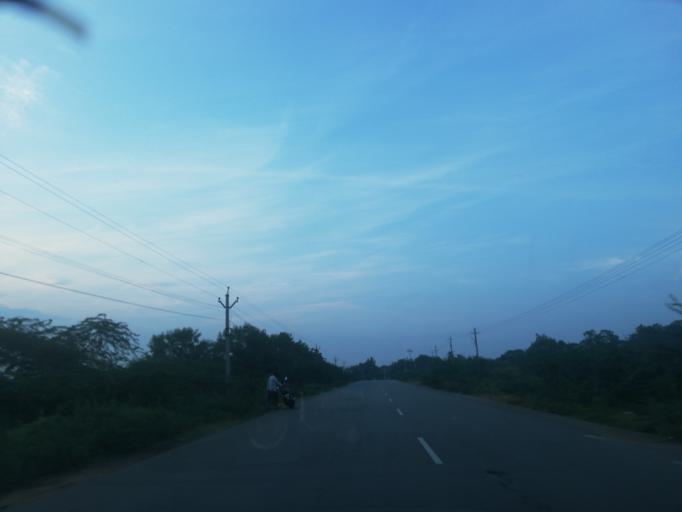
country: IN
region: Andhra Pradesh
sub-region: Guntur
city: Macherla
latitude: 16.5943
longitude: 79.3148
